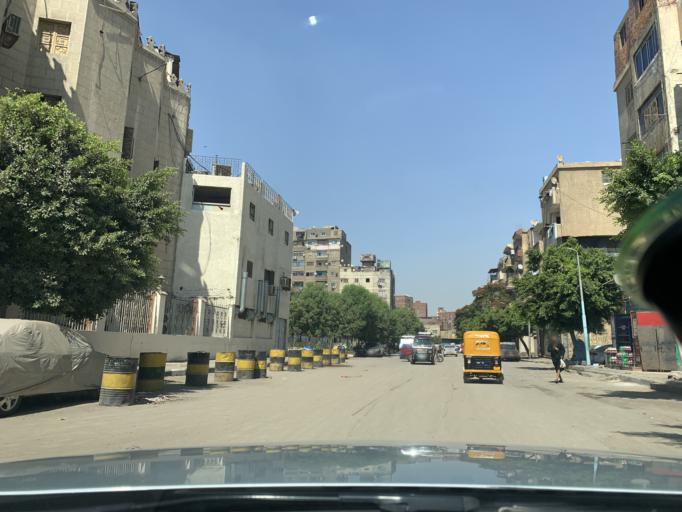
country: EG
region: Muhafazat al Qahirah
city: Cairo
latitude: 30.0781
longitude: 31.2593
